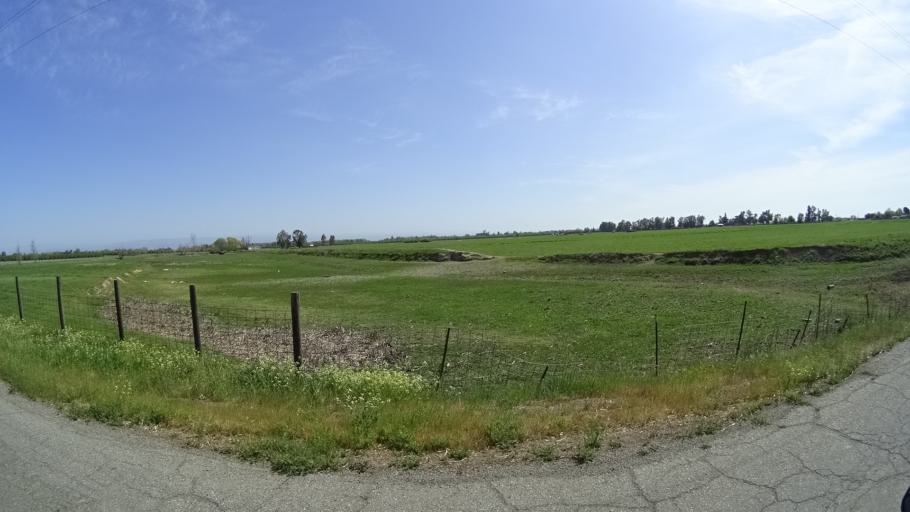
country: US
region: California
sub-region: Glenn County
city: Hamilton City
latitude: 39.8023
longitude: -122.0857
